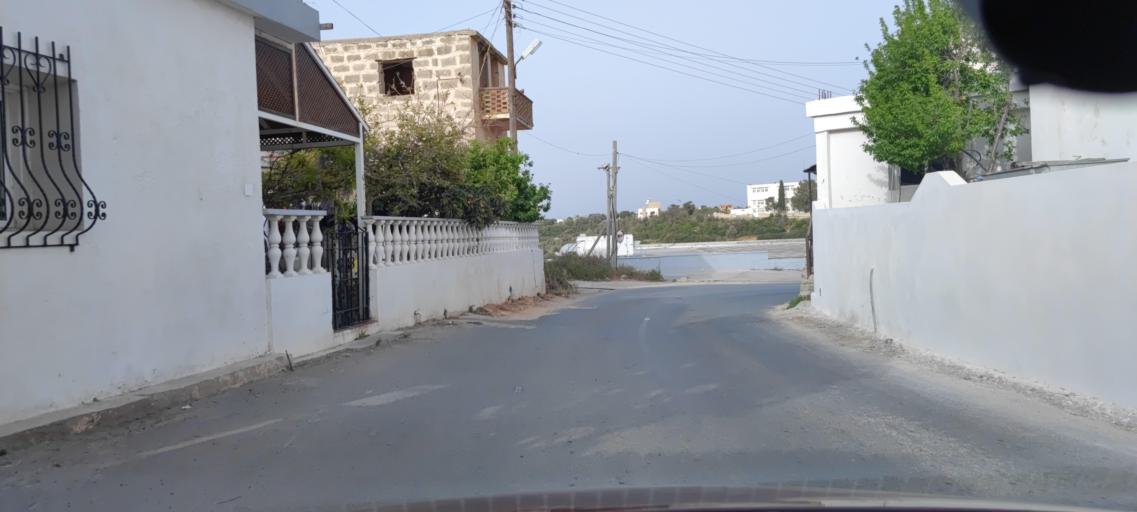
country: CY
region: Ammochostos
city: Leonarisso
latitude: 35.5367
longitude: 34.1911
